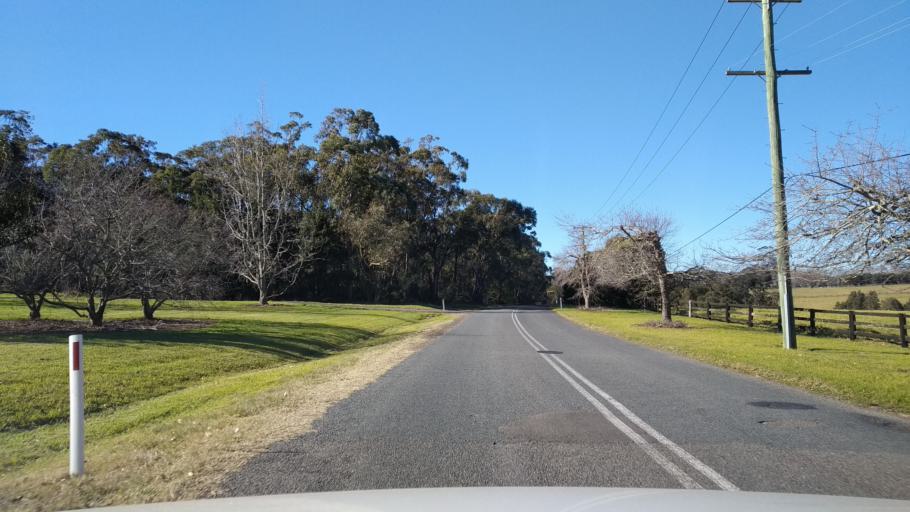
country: AU
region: New South Wales
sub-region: Wyong Shire
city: Little Jilliby
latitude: -33.2436
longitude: 151.2198
